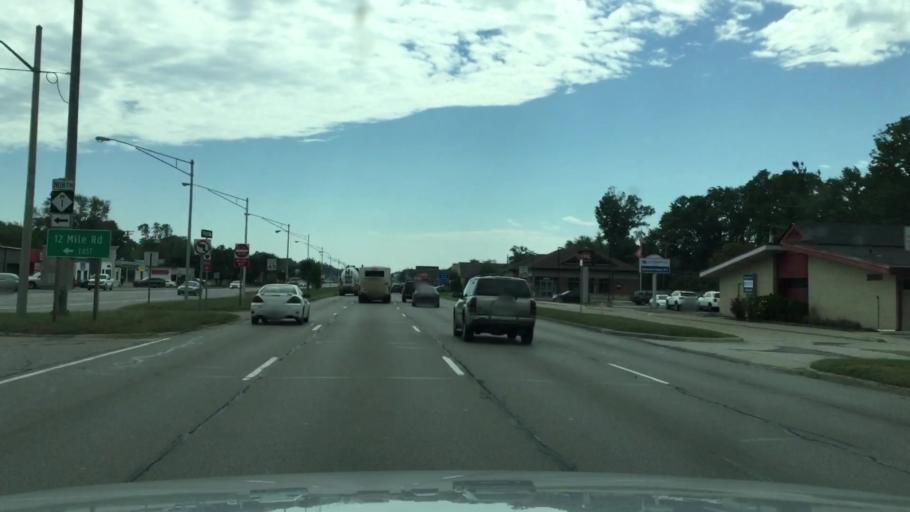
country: US
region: Michigan
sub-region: Oakland County
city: Berkley
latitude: 42.5017
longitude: -83.1707
